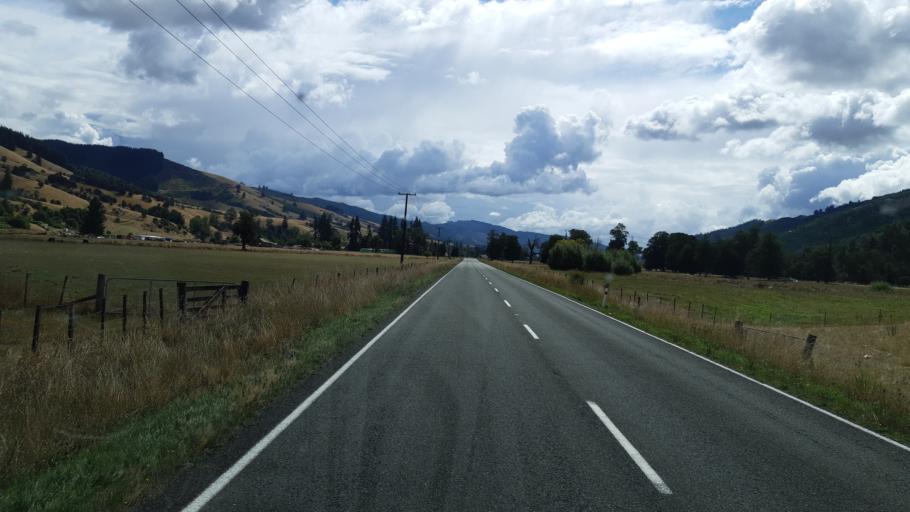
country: NZ
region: Tasman
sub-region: Tasman District
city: Wakefield
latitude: -41.5244
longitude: 172.7957
